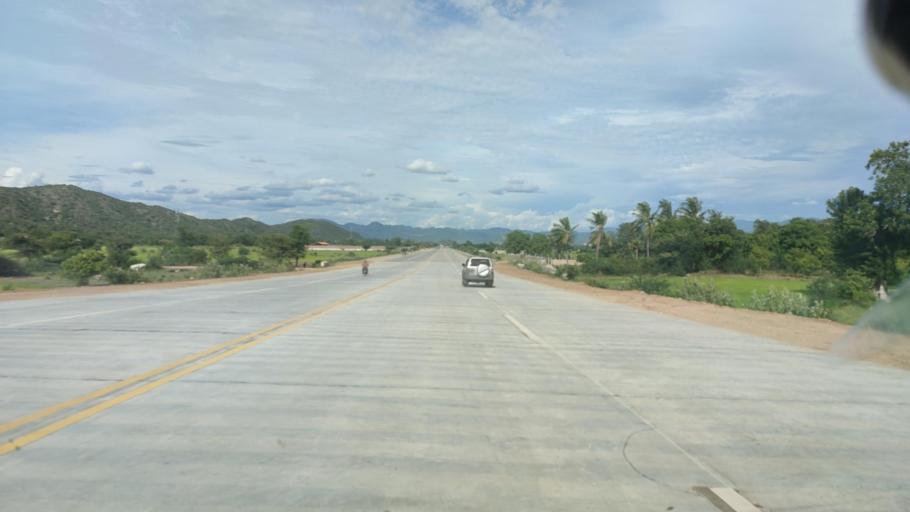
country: MM
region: Mandalay
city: Kyaukse
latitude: 21.5931
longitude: 96.1534
